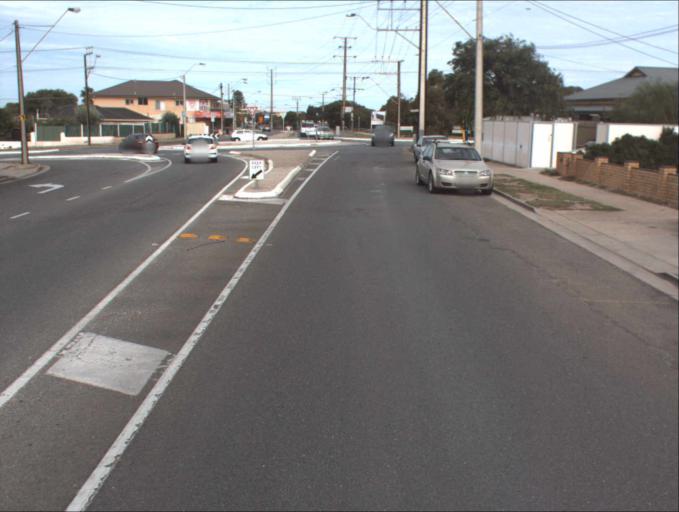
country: AU
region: South Australia
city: Port Adelaide
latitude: -34.8497
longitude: 138.4796
